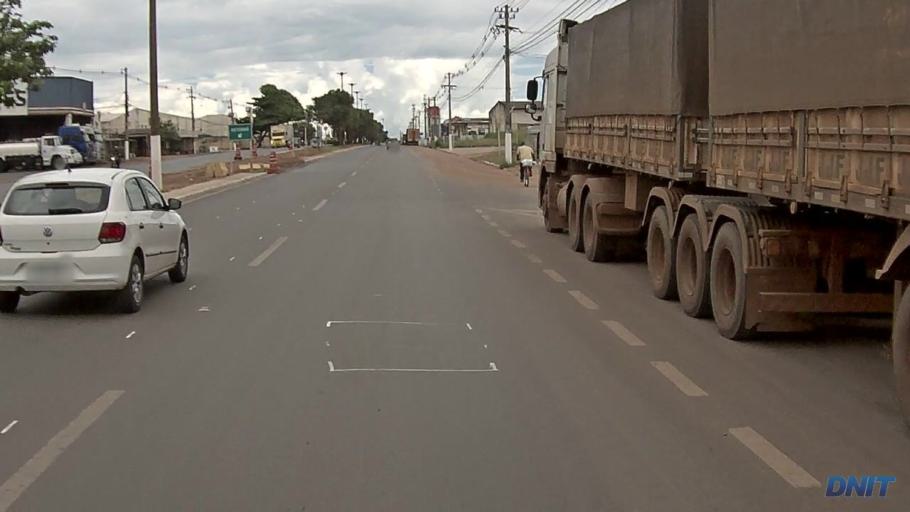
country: BR
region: Mato Grosso
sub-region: Varzea Grande
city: Varzea Grande
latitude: -15.6434
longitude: -56.1811
